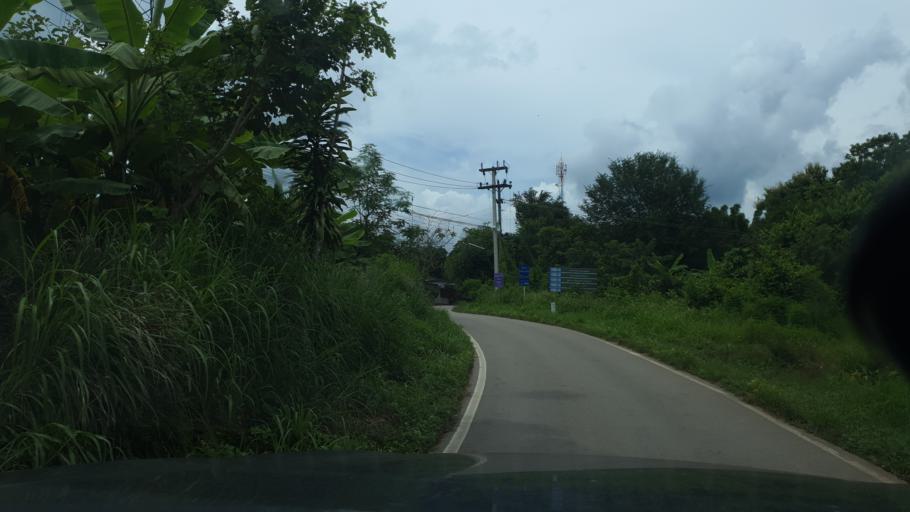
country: TH
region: Lampang
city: Hang Chat
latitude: 18.4076
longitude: 99.2619
